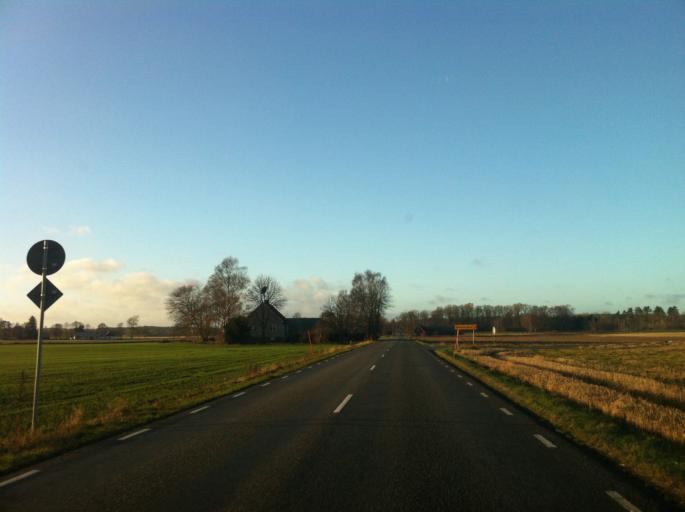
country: SE
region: Skane
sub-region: Ostra Goinge Kommun
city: Knislinge
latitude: 56.1877
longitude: 14.0169
